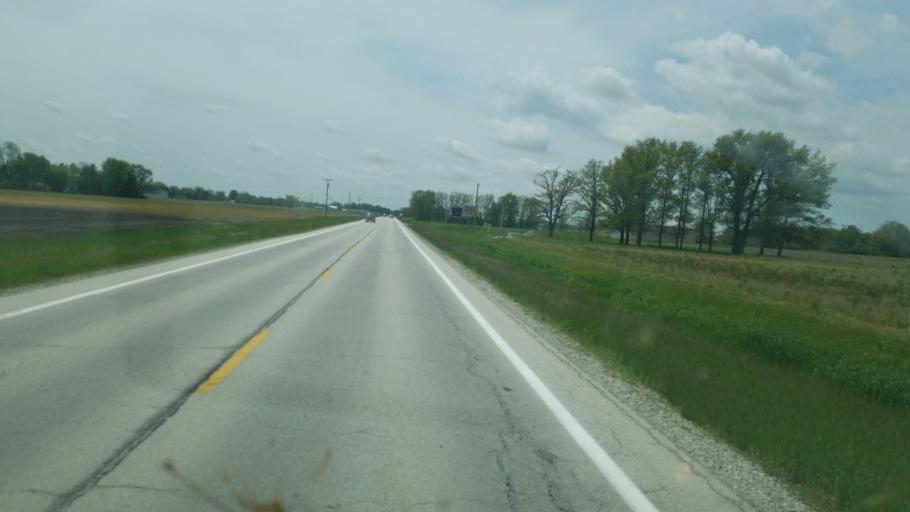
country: US
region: Ohio
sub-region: Sandusky County
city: Fremont
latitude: 41.4311
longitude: -83.0759
